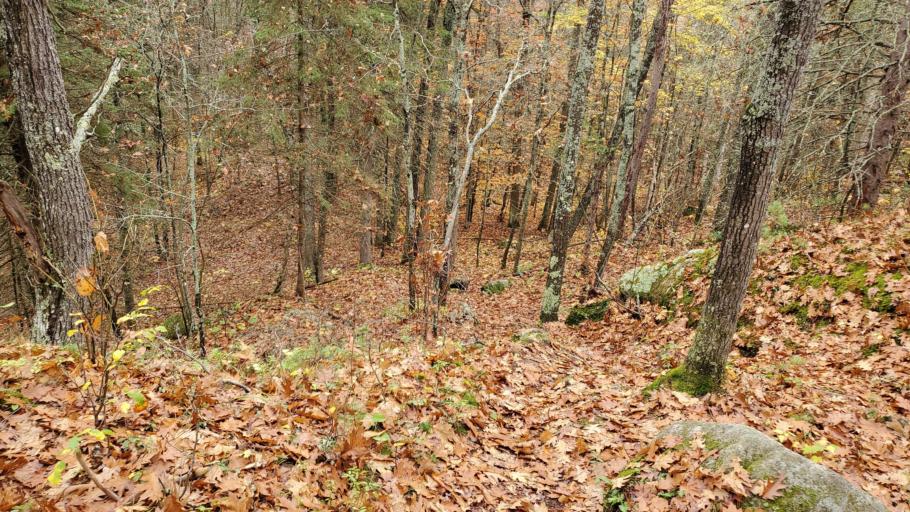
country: CA
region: Ontario
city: Renfrew
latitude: 45.2617
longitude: -77.1798
